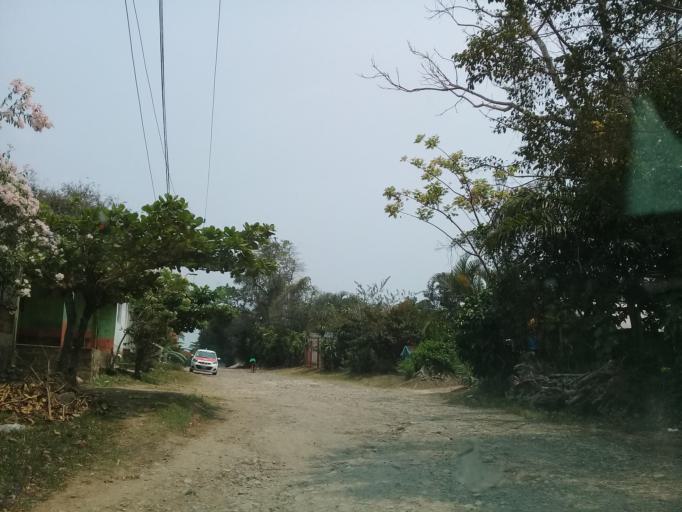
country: MX
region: Veracruz
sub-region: Tezonapa
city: Laguna Chica (Pueblo Nuevo)
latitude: 18.5461
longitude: -96.7354
